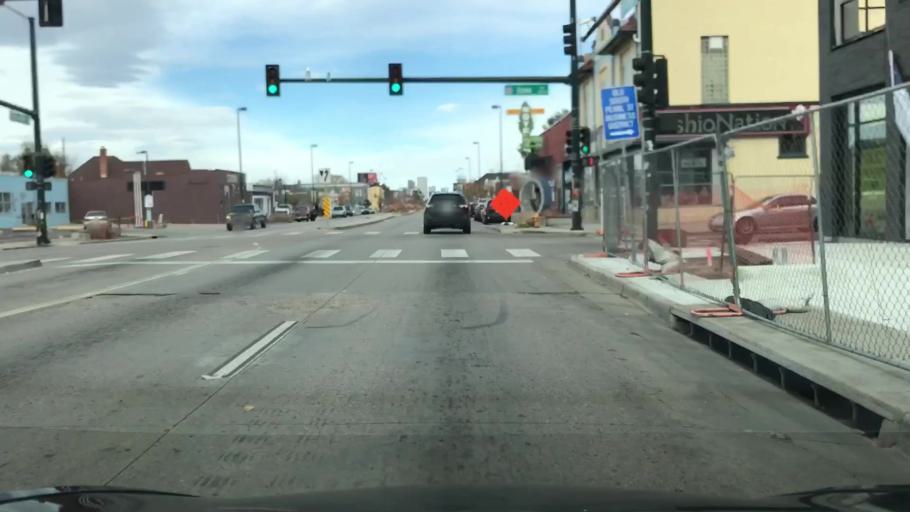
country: US
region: Colorado
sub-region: Arapahoe County
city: Englewood
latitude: 39.6874
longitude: -104.9874
